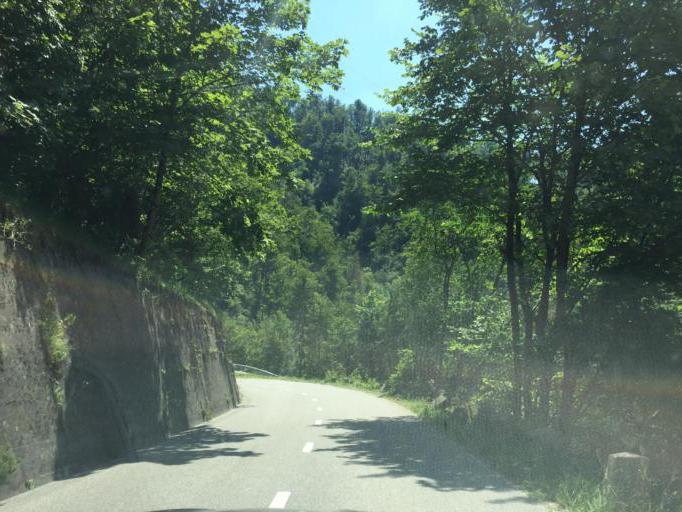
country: SI
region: Idrija
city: Spodnja Idrija
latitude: 46.0317
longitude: 14.0409
